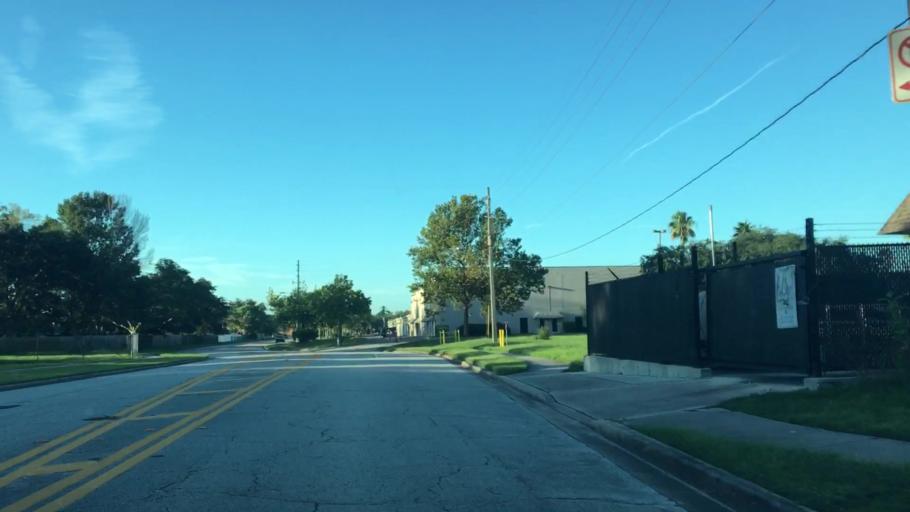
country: US
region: Florida
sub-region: Orange County
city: Conway
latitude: 28.4843
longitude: -81.3070
